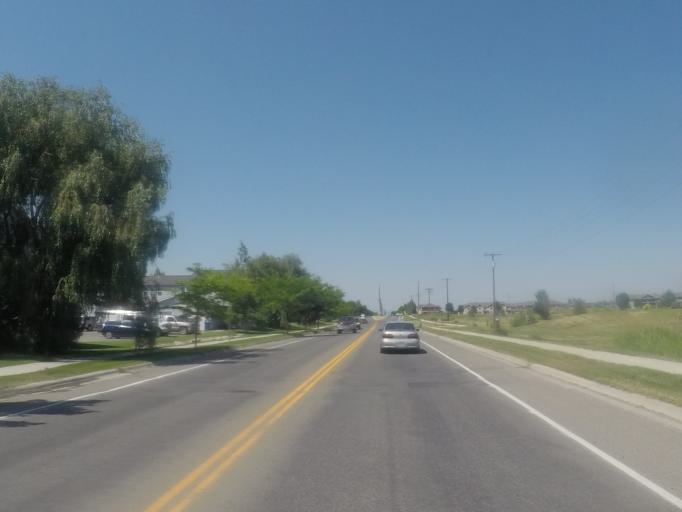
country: US
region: Montana
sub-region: Gallatin County
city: Bozeman
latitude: 45.6930
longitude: -111.0678
